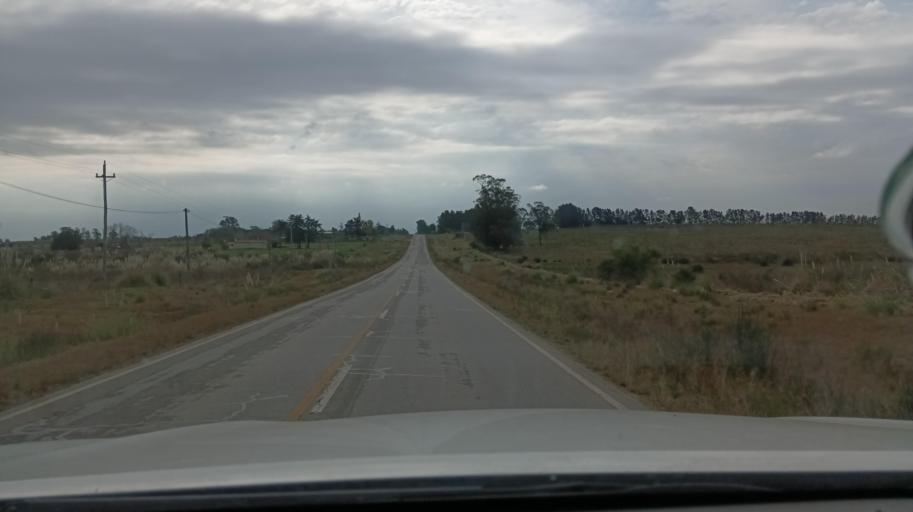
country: UY
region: Canelones
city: Sauce
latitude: -34.6426
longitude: -56.1066
